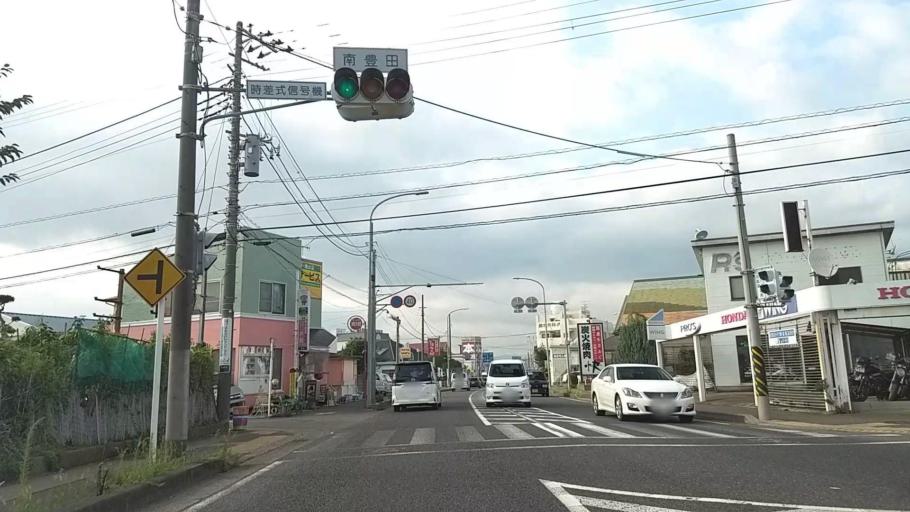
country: JP
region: Kanagawa
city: Hiratsuka
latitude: 35.3557
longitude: 139.3274
